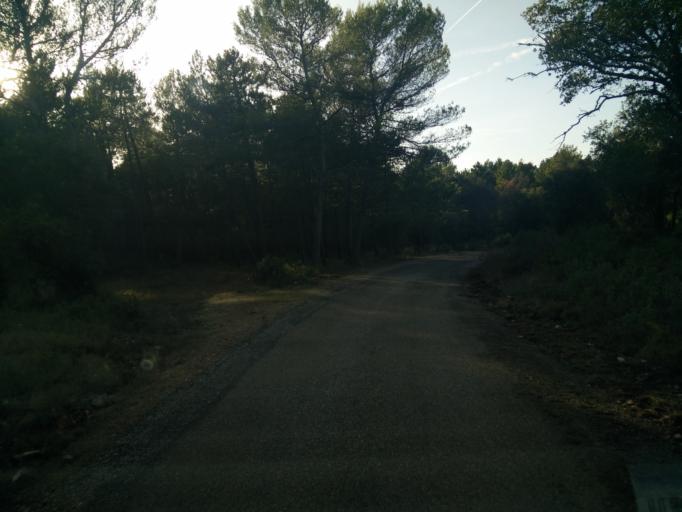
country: FR
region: Provence-Alpes-Cote d'Azur
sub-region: Departement du Var
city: Signes
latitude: 43.2384
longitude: 5.8826
